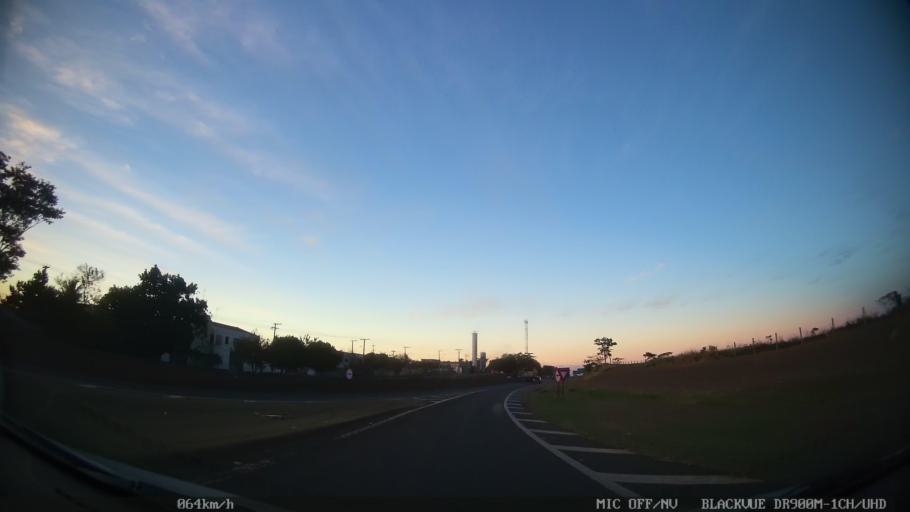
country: BR
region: Sao Paulo
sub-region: Catanduva
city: Catanduva
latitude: -21.1326
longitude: -49.0176
